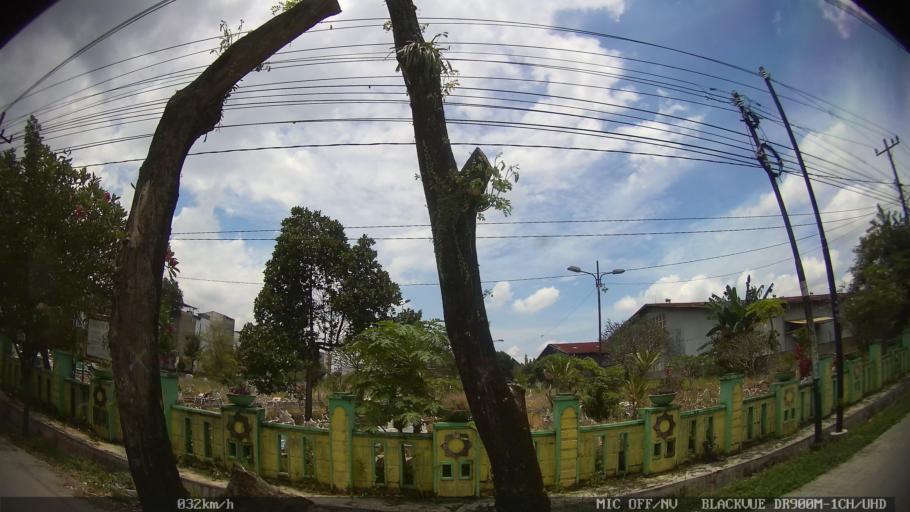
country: ID
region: North Sumatra
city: Medan
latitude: 3.6261
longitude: 98.6772
